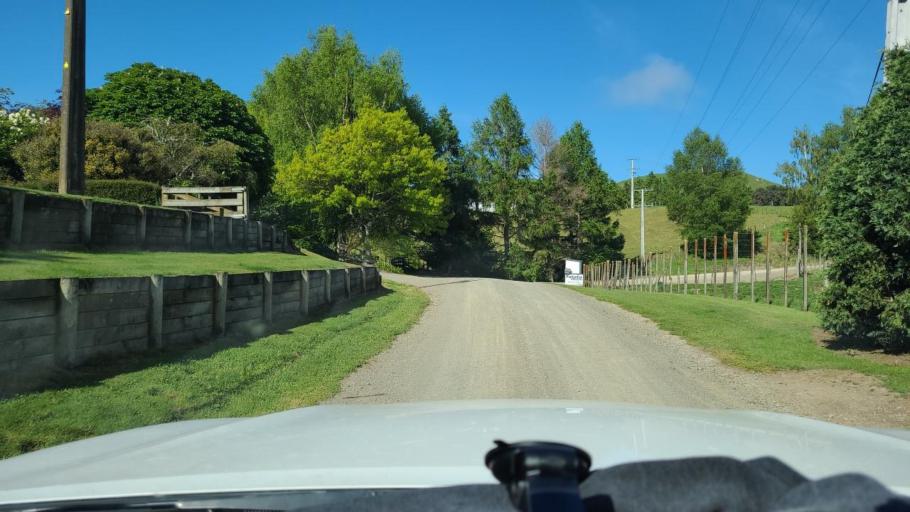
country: NZ
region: Bay of Plenty
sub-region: Opotiki District
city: Opotiki
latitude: -38.4617
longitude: 177.3838
